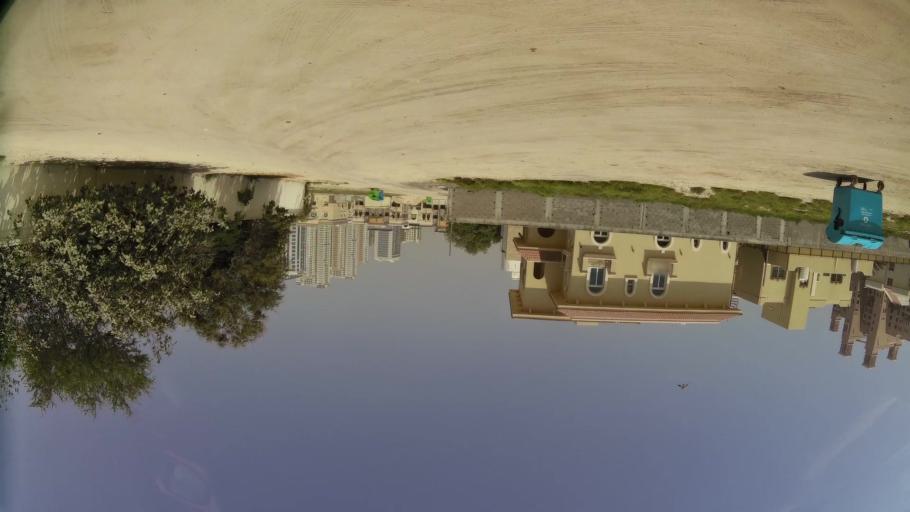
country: AE
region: Ajman
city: Ajman
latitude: 25.3935
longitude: 55.4227
